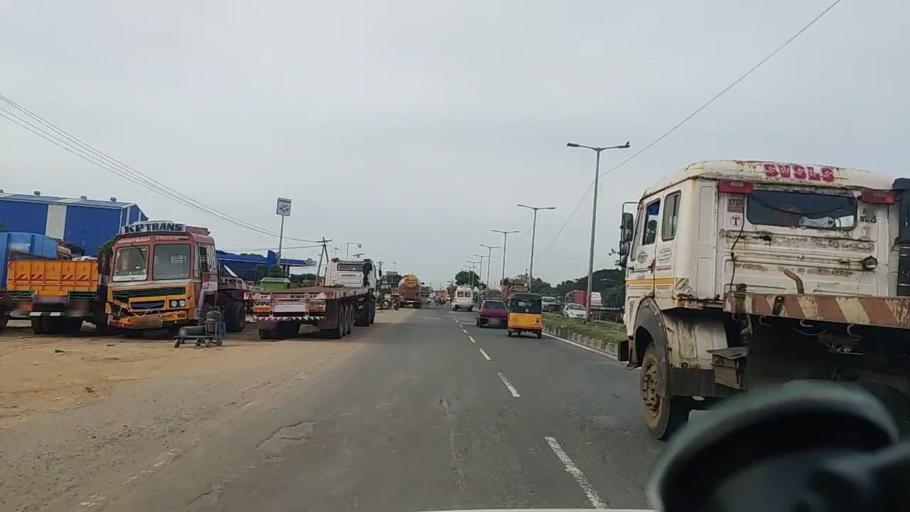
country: IN
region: Tamil Nadu
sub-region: Thiruvallur
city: Chinnasekkadu
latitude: 13.1609
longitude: 80.2268
